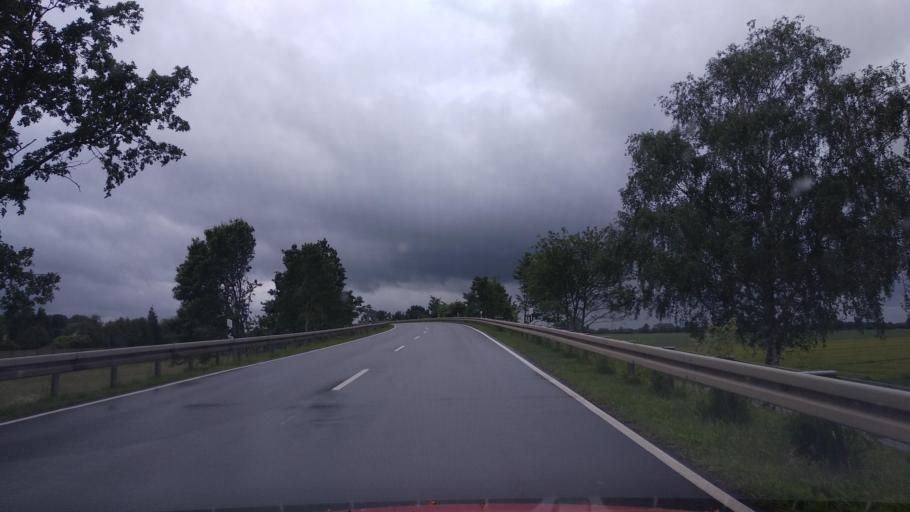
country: DE
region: Lower Saxony
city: Lauenhagen
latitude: 52.3424
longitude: 9.2316
